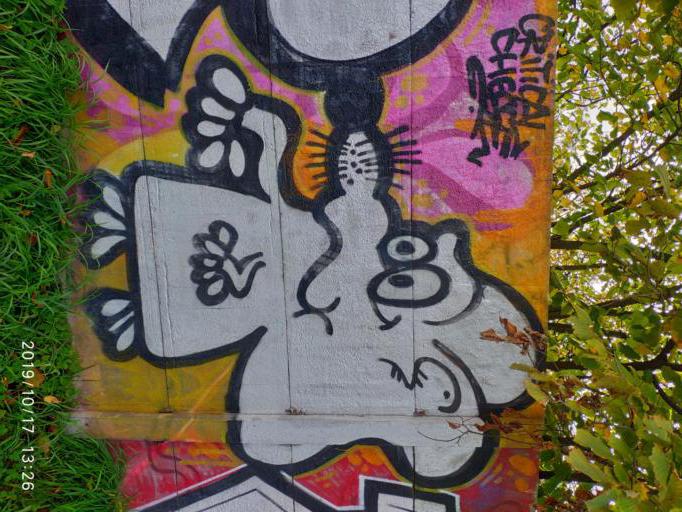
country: PL
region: Lubusz
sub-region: Zielona Gora
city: Zielona Gora
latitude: 51.9463
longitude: 15.5355
